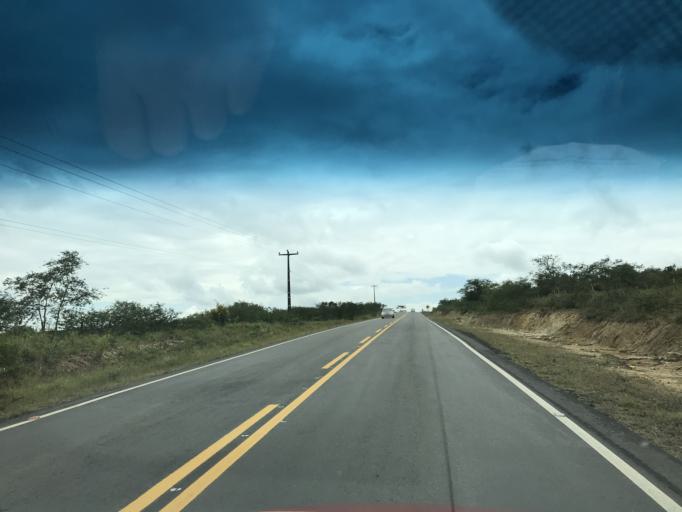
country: BR
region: Bahia
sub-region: Conceicao Do Almeida
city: Conceicao do Almeida
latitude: -12.6684
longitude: -39.2864
